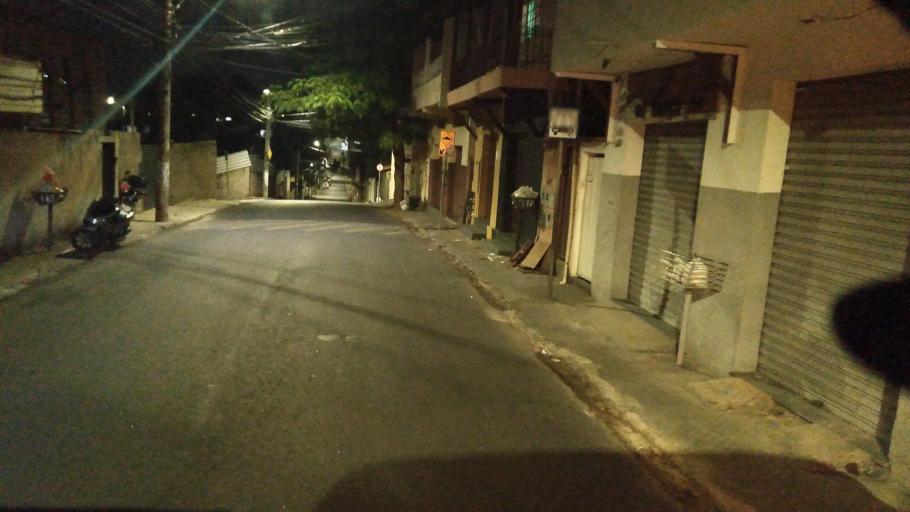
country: BR
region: Minas Gerais
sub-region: Belo Horizonte
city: Belo Horizonte
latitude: -19.8929
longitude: -43.9616
